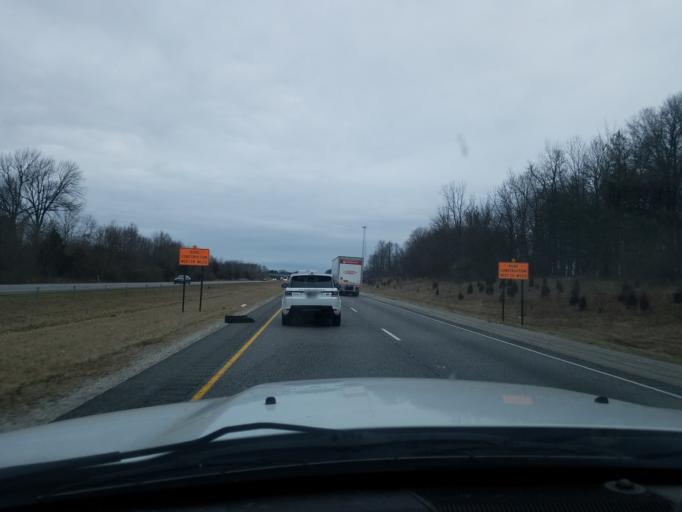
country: US
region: Indiana
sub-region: Tippecanoe County
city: Dayton
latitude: 40.3390
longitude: -86.7620
